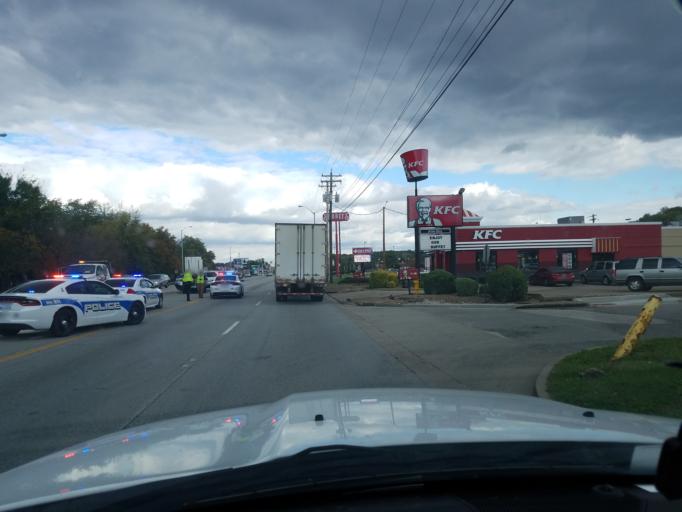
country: US
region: Kentucky
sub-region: Henderson County
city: Henderson
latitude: 37.8696
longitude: -87.5708
